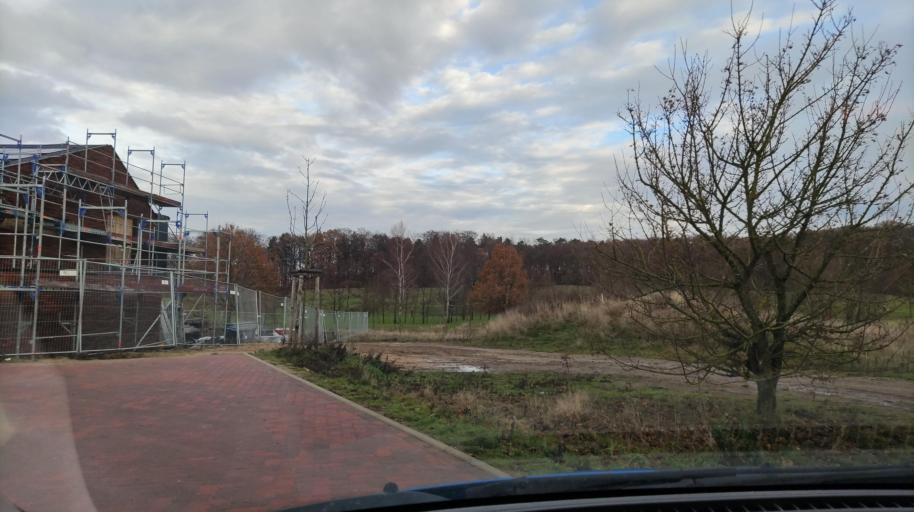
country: DE
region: Lower Saxony
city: Adendorf
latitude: 53.2926
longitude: 10.4520
